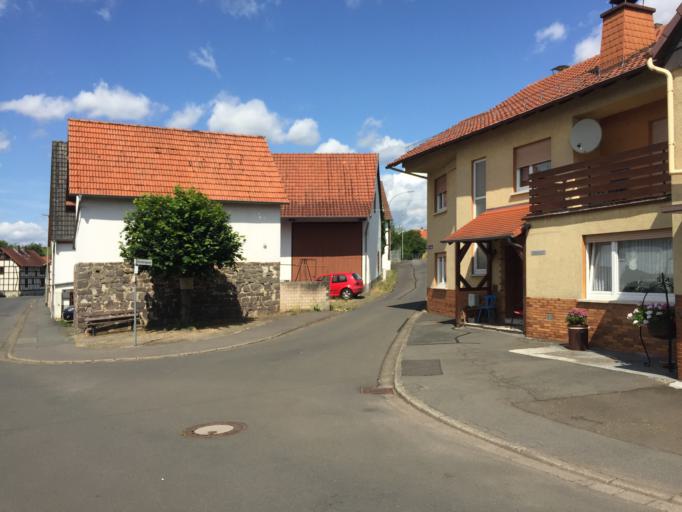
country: DE
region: Hesse
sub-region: Regierungsbezirk Giessen
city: Grunberg
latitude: 50.5709
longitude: 8.9719
